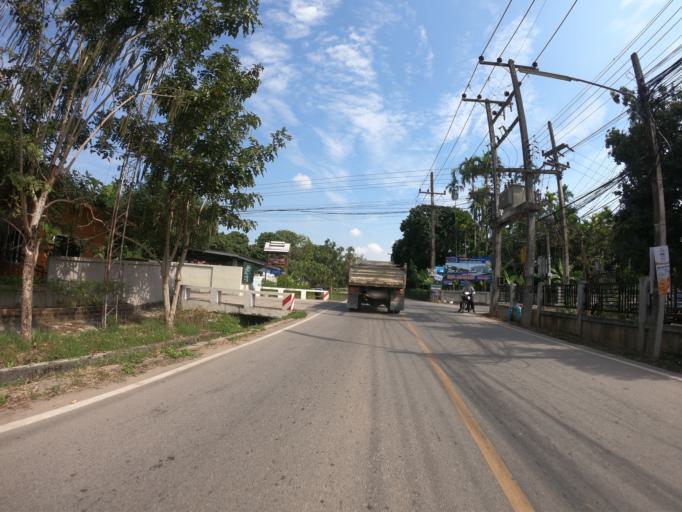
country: TH
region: Chiang Mai
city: San Sai
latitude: 18.8623
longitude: 99.0593
